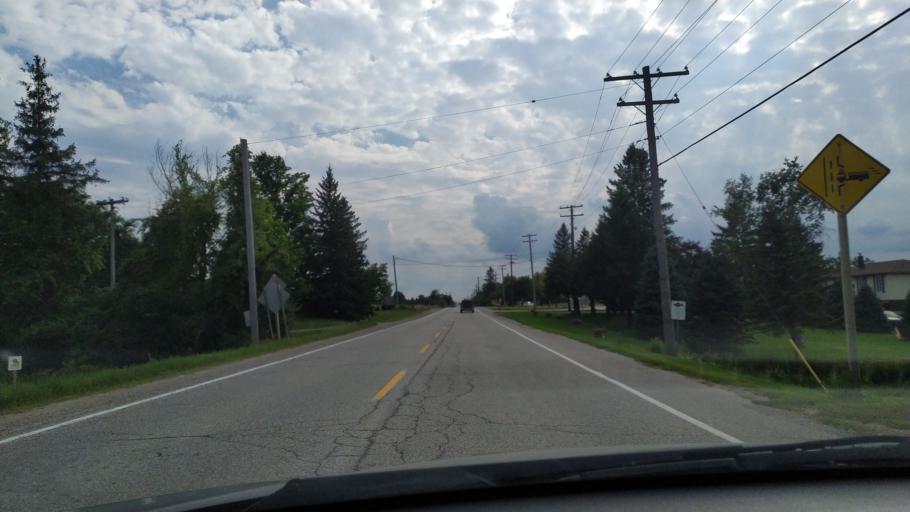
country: CA
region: Ontario
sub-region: Wellington County
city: Guelph
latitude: 43.4722
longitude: -80.1560
